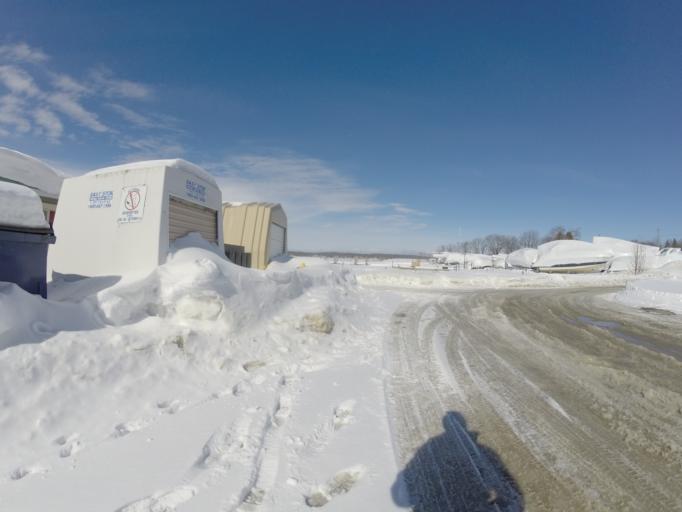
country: CA
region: Ontario
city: Midland
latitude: 44.7531
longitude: -79.8875
